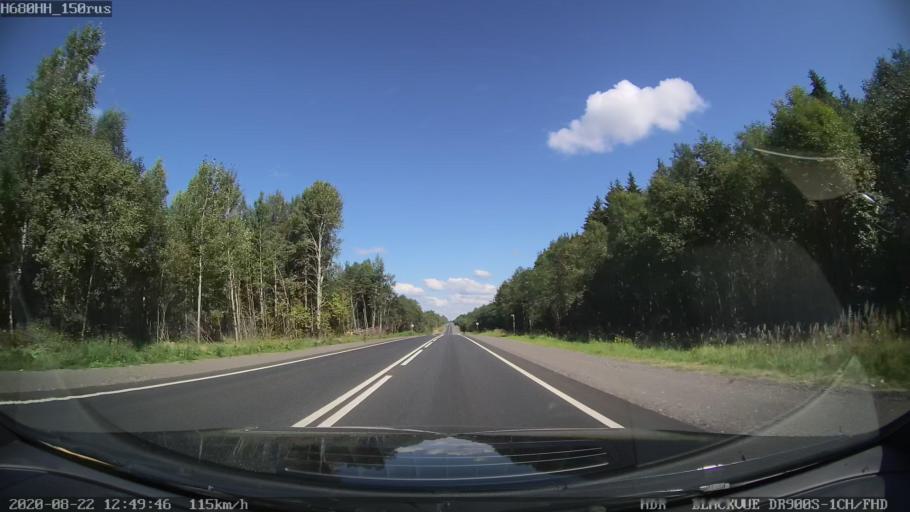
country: RU
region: Tverskaya
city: Rameshki
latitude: 57.4564
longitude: 36.2112
